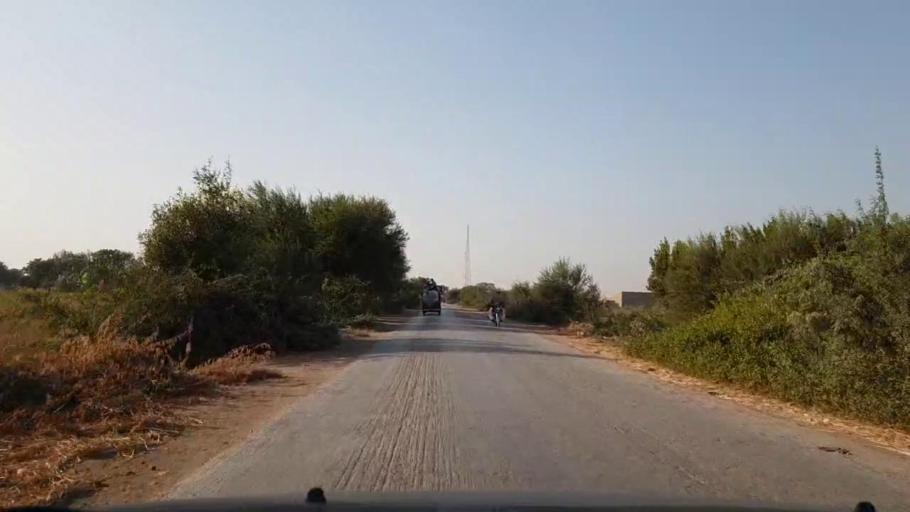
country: PK
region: Sindh
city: Chambar
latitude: 25.2096
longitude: 68.7827
